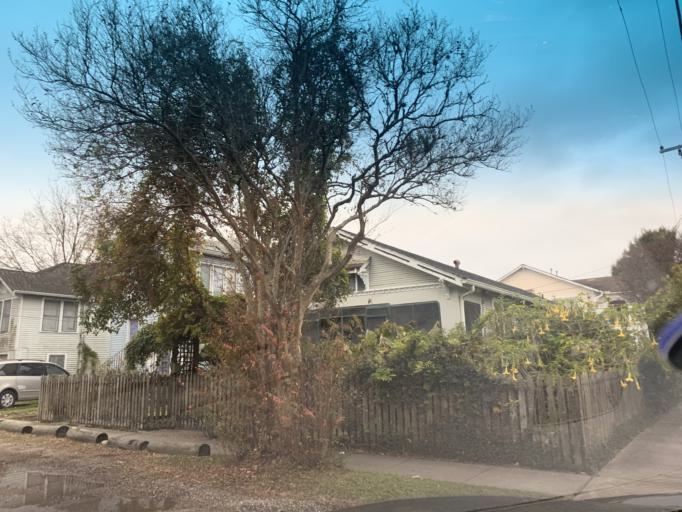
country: US
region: Louisiana
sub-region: Orleans Parish
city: New Orleans
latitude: 29.9838
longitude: -90.1083
